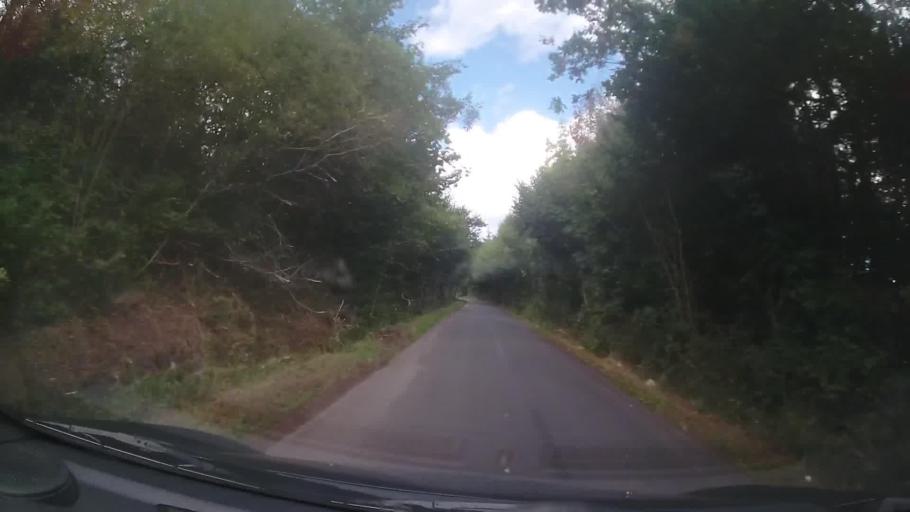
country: GB
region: Wales
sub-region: Merthyr Tydfil County Borough
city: Merthyr Tydfil
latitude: 51.8142
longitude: -3.3743
